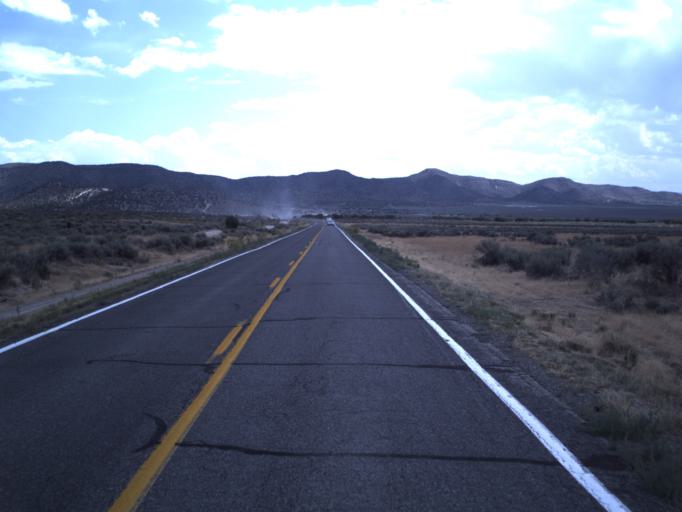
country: US
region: Utah
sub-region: Utah County
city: Eagle Mountain
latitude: 40.2378
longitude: -112.2013
